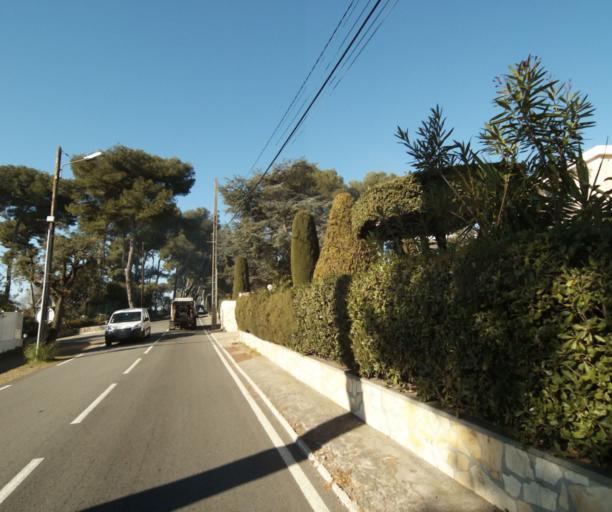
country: FR
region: Provence-Alpes-Cote d'Azur
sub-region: Departement des Alpes-Maritimes
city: Biot
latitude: 43.6044
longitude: 7.0943
